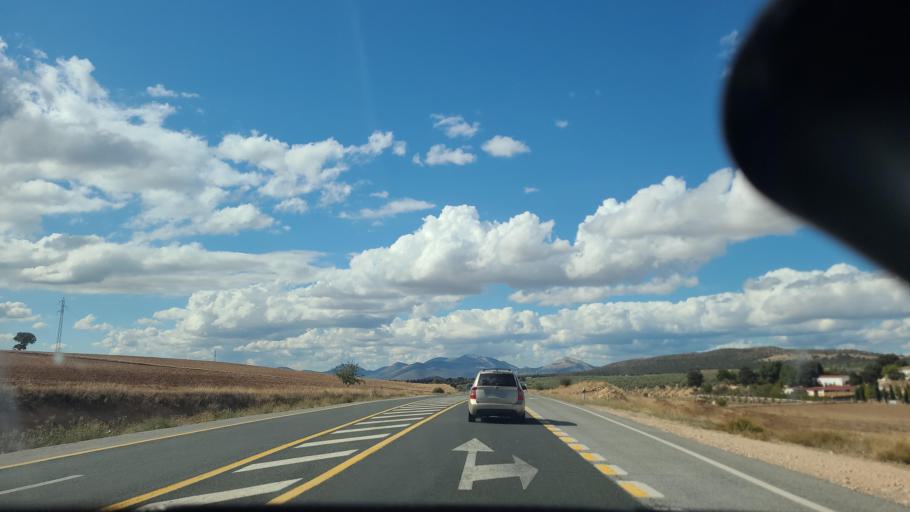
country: ES
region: Andalusia
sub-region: Provincia de Granada
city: Pinar
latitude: 37.3972
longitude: -3.4228
